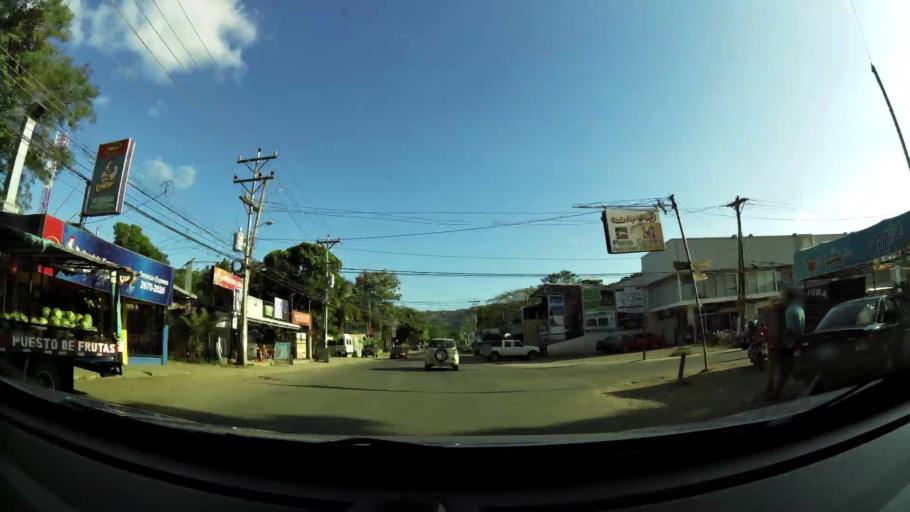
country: CR
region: Guanacaste
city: Sardinal
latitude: 10.5491
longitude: -85.6960
